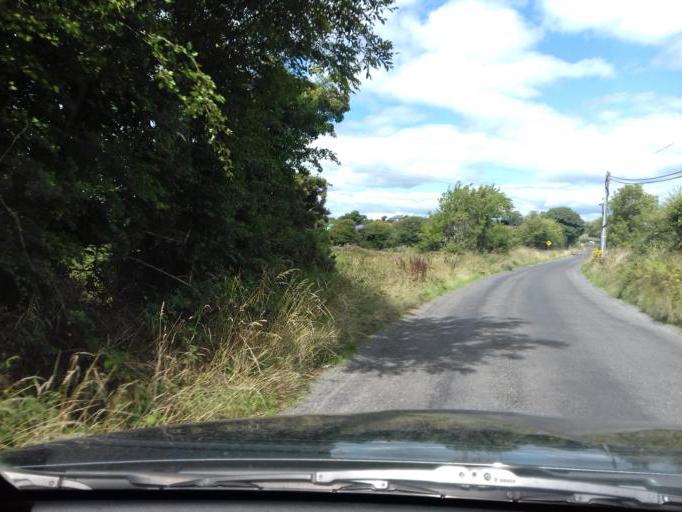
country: IE
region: Munster
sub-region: Waterford
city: Tra Mhor
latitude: 52.1782
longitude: -7.2376
